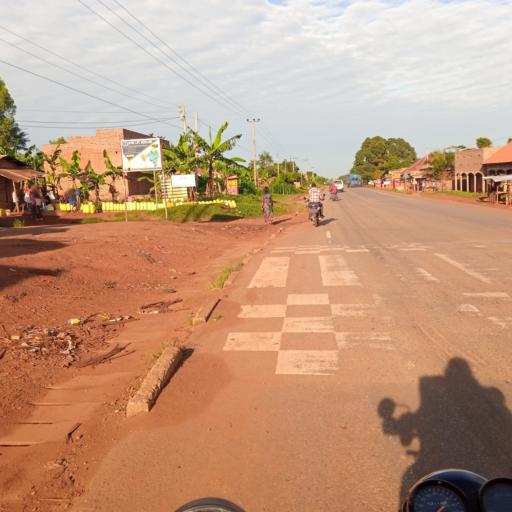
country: UG
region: Eastern Region
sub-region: Mbale District
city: Mbale
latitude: 1.1484
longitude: 34.1991
